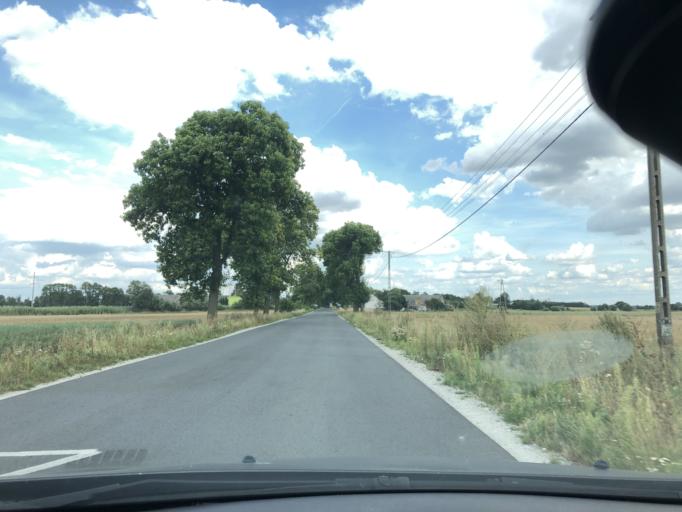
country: PL
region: Lodz Voivodeship
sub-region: Powiat wieruszowski
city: Czastary
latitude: 51.2418
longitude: 18.3572
